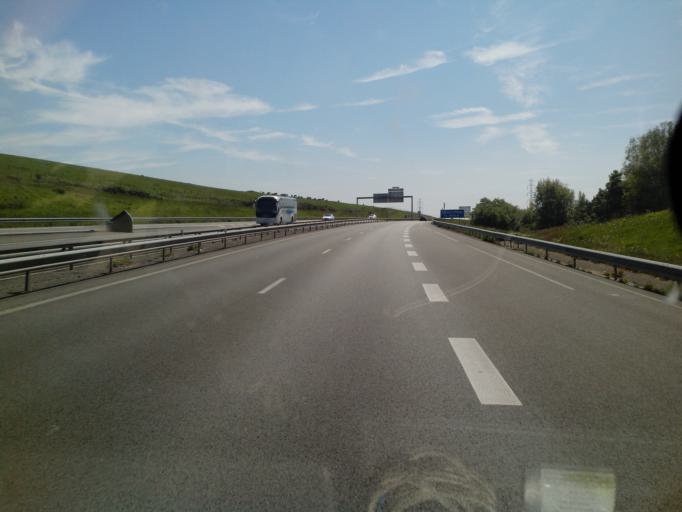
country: FR
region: Nord-Pas-de-Calais
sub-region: Departement du Pas-de-Calais
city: Saint-Martin-Boulogne
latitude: 50.7178
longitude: 1.6469
